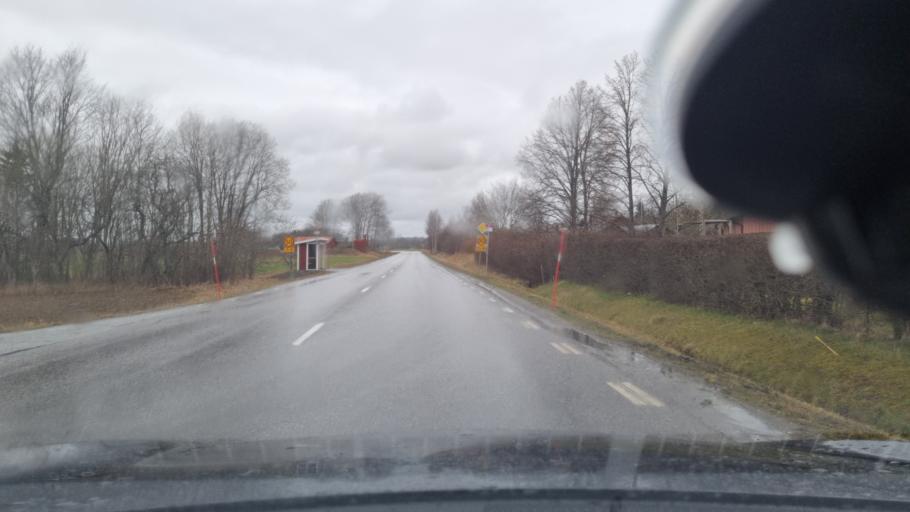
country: SE
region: Stockholm
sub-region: Sigtuna Kommun
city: Sigtuna
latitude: 59.5861
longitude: 17.6611
